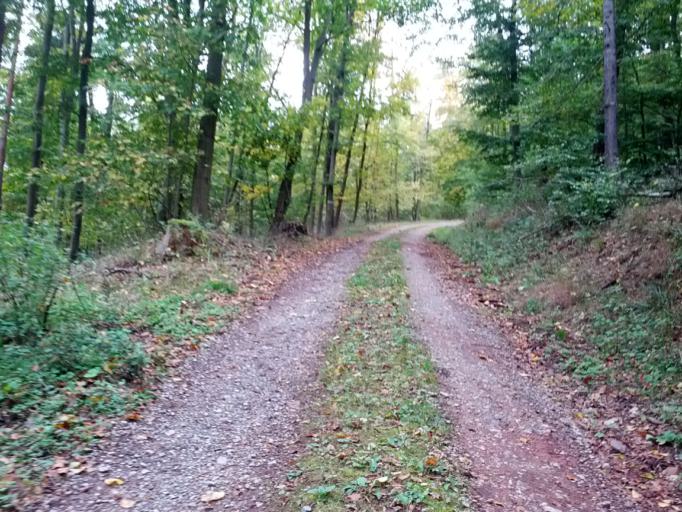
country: DE
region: Thuringia
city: Eisenach
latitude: 50.9667
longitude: 10.2894
